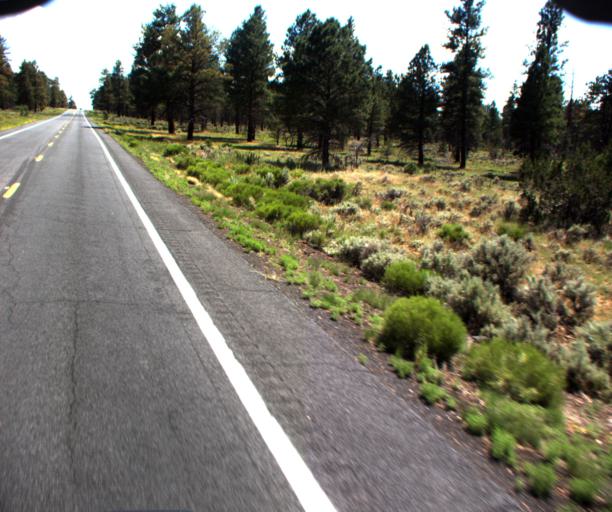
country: US
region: Arizona
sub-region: Coconino County
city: Grand Canyon Village
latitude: 35.9135
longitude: -112.1298
